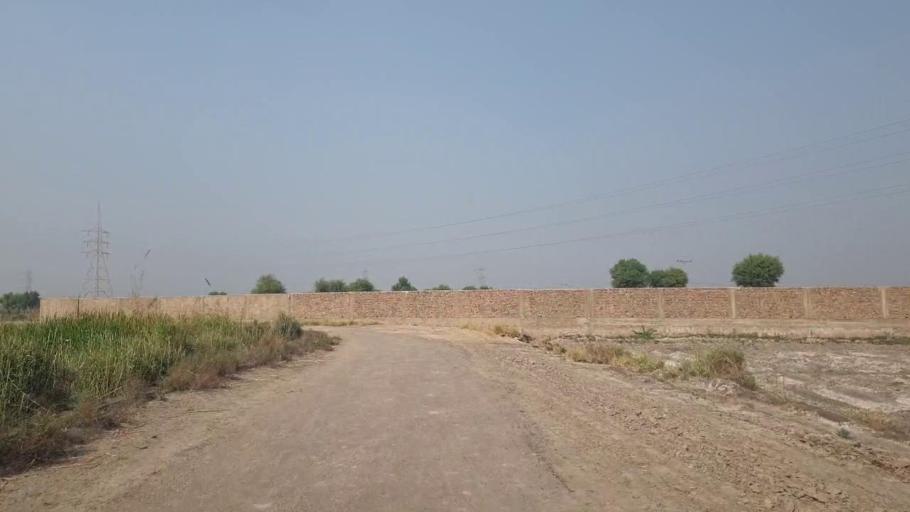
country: PK
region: Sindh
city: Jamshoro
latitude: 25.4553
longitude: 68.3336
